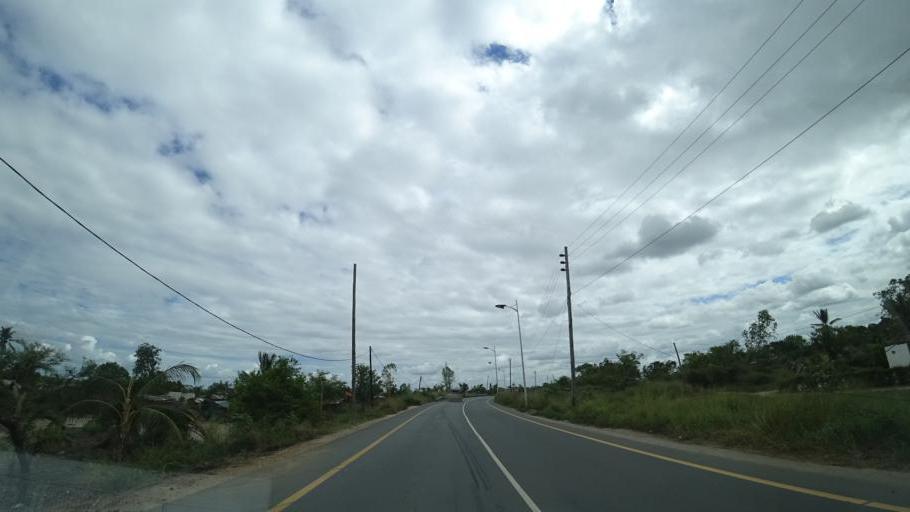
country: MZ
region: Sofala
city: Dondo
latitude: -19.4987
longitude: 34.5945
